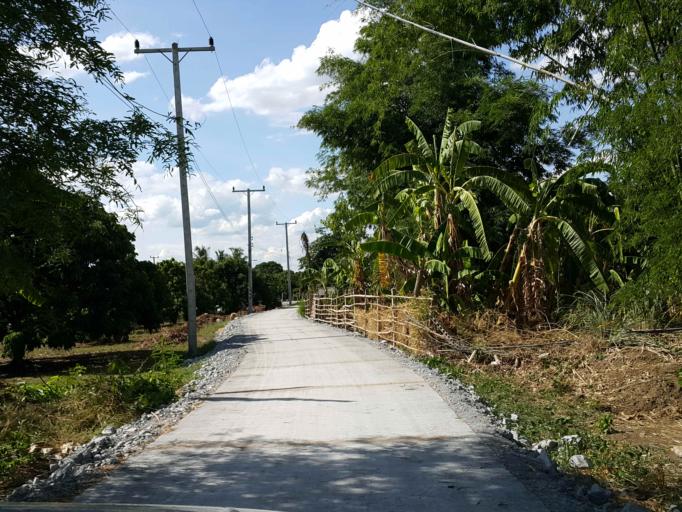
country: TH
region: Chiang Mai
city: San Kamphaeng
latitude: 18.8009
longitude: 99.1482
